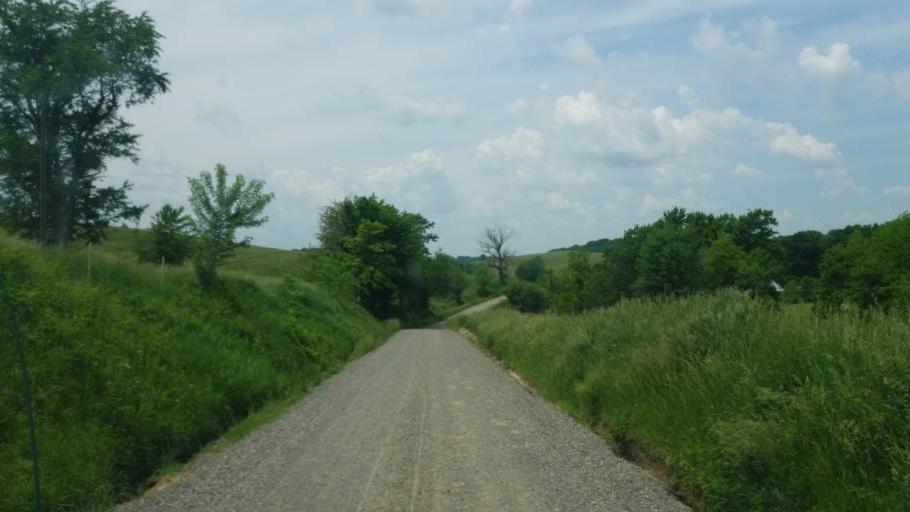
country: US
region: Ohio
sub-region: Holmes County
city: Millersburg
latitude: 40.4817
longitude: -81.7905
